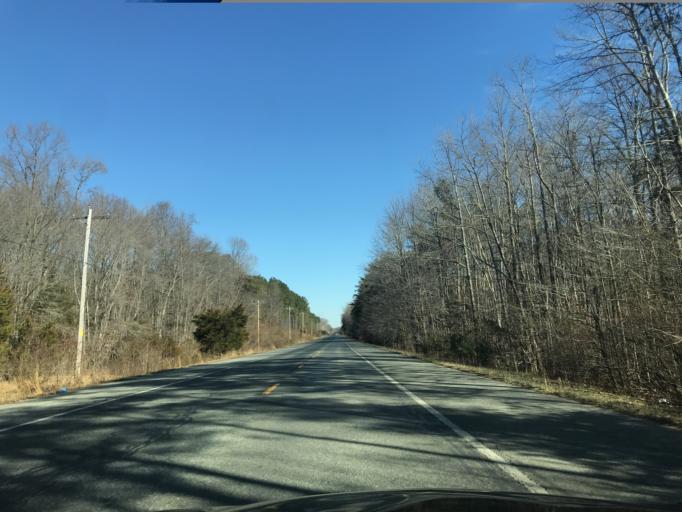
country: US
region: Virginia
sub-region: Prince William County
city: Cherry Hill
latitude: 38.5327
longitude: -77.2068
